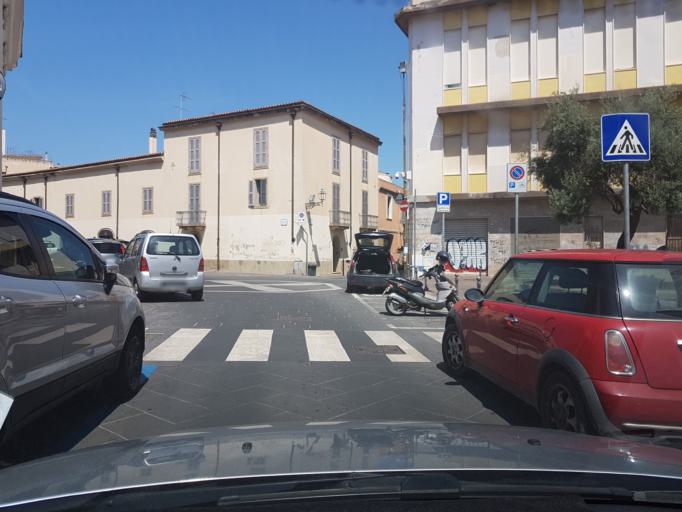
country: IT
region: Sardinia
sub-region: Provincia di Oristano
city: Oristano
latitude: 39.9037
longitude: 8.5905
